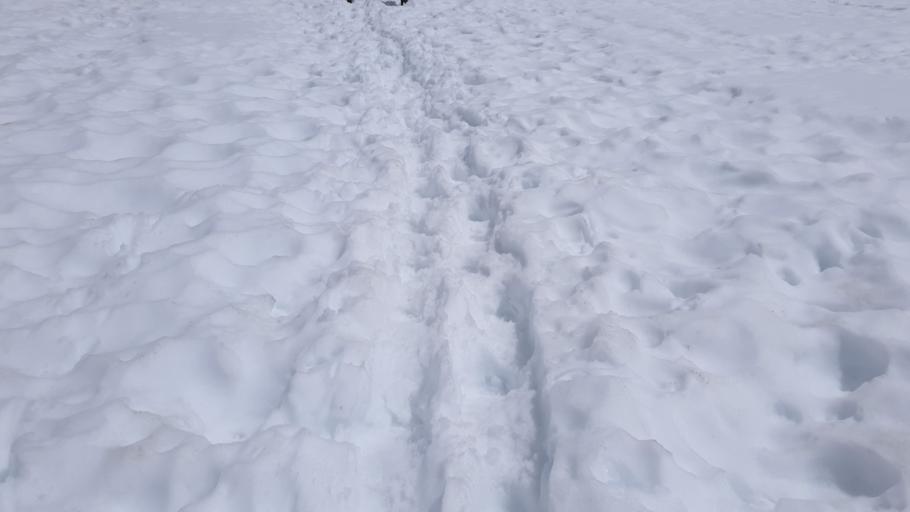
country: IT
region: Trentino-Alto Adige
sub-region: Bolzano
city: Sesto
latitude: 46.6224
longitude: 12.3133
